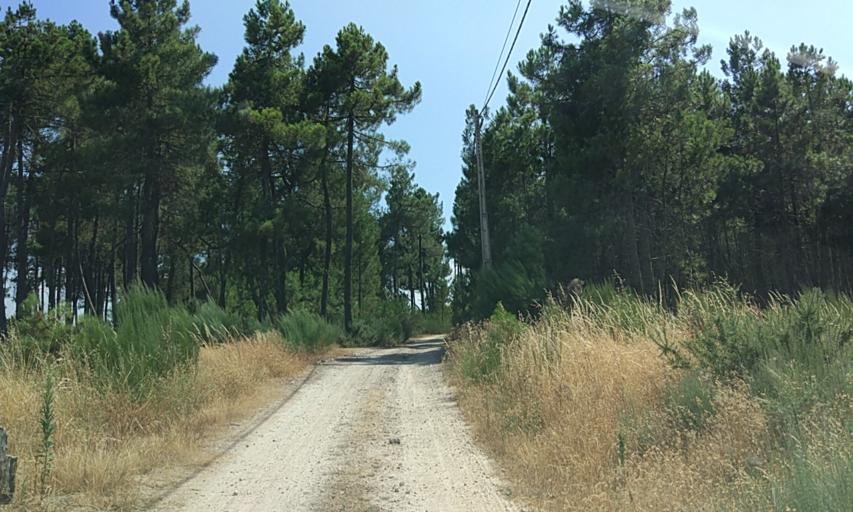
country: PT
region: Vila Real
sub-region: Murca
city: Murca
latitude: 41.3450
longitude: -7.4737
